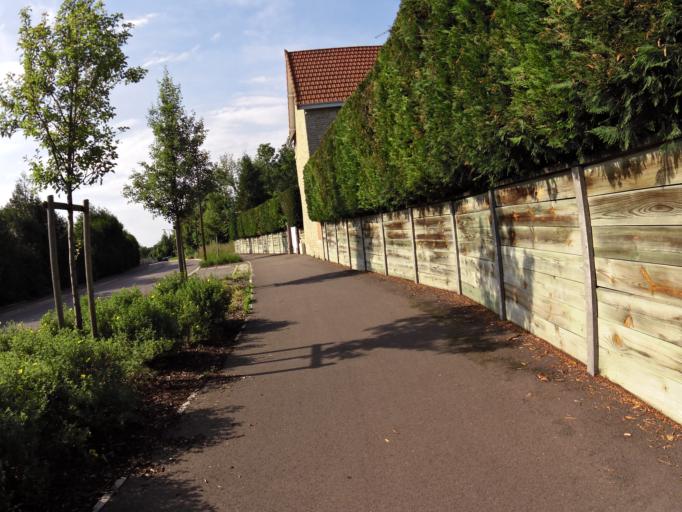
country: FR
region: Champagne-Ardenne
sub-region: Departement de l'Aube
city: Saint-Julien-les-Villas
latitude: 48.2796
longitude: 4.0994
